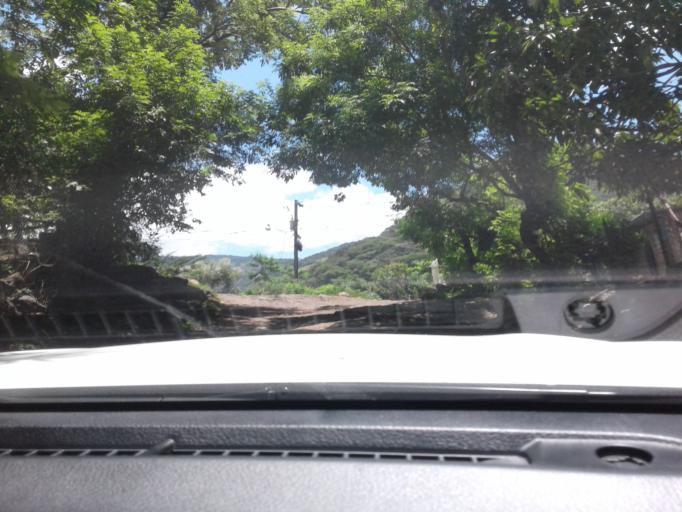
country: NI
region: Matagalpa
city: Terrabona
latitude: 12.8325
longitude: -85.9862
